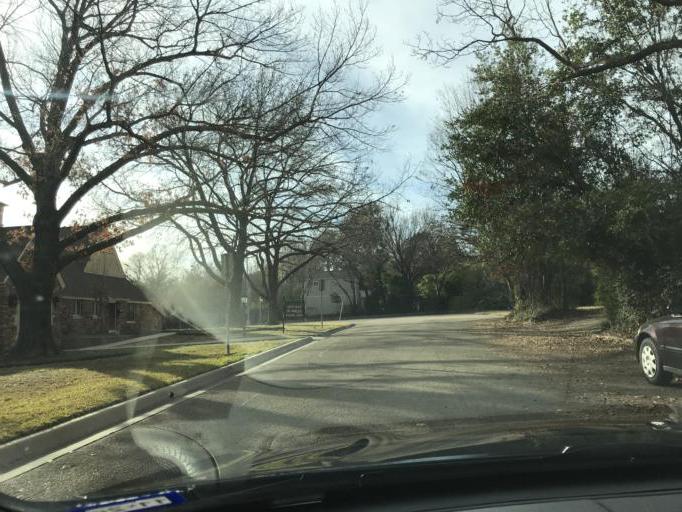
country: US
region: Texas
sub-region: Denton County
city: Denton
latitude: 33.2201
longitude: -97.1554
